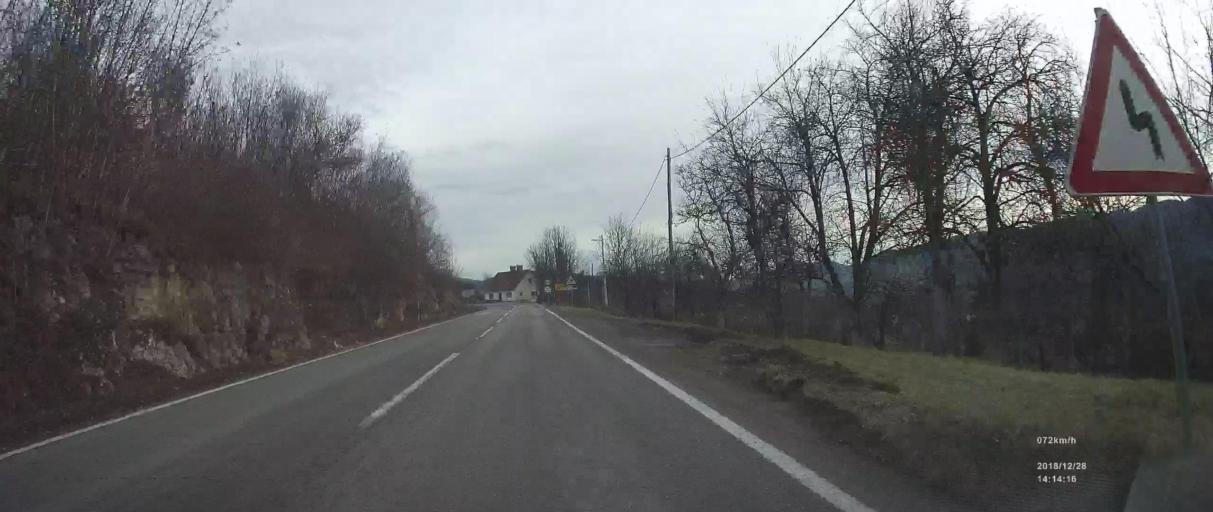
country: HR
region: Primorsko-Goranska
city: Vrbovsko
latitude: 45.4323
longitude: 15.0171
